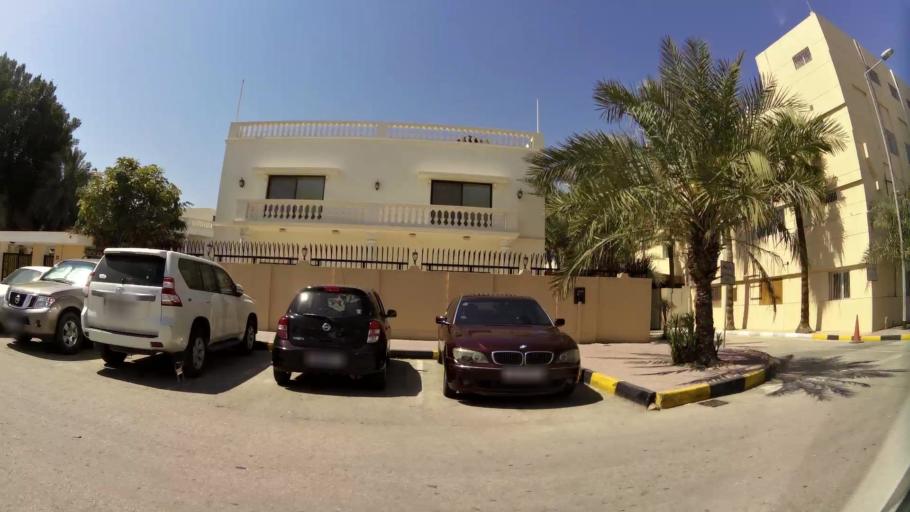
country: BH
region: Manama
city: Manama
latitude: 26.2215
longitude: 50.5912
